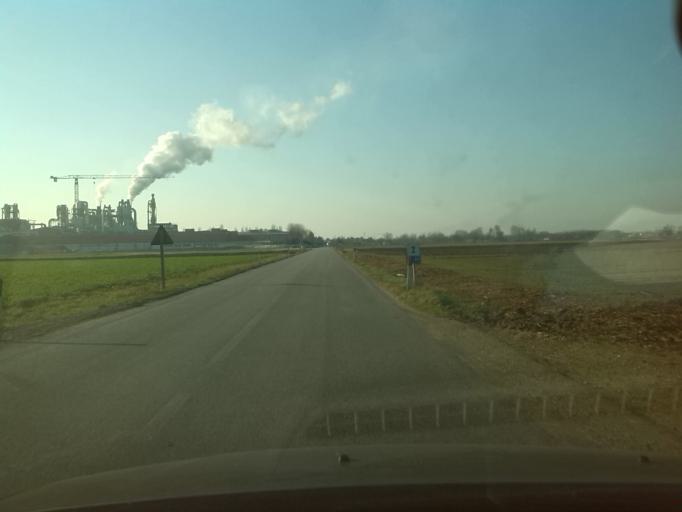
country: IT
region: Friuli Venezia Giulia
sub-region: Provincia di Udine
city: Bicinicco
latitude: 45.9306
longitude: 13.2667
